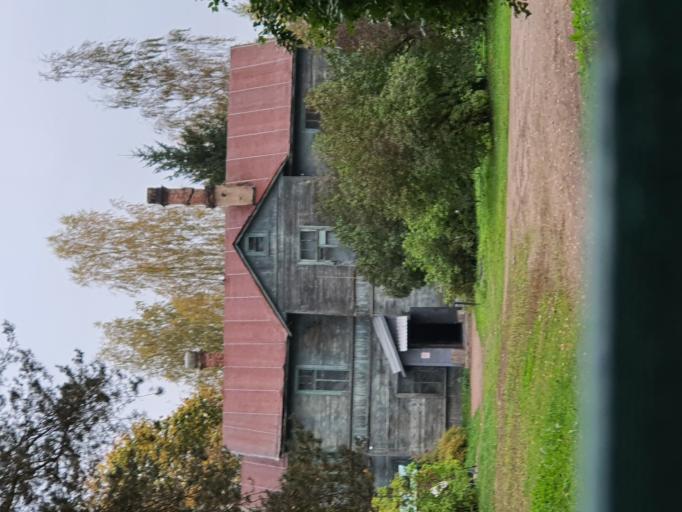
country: RU
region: St.-Petersburg
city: Pavlovsk
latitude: 59.6892
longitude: 30.4438
